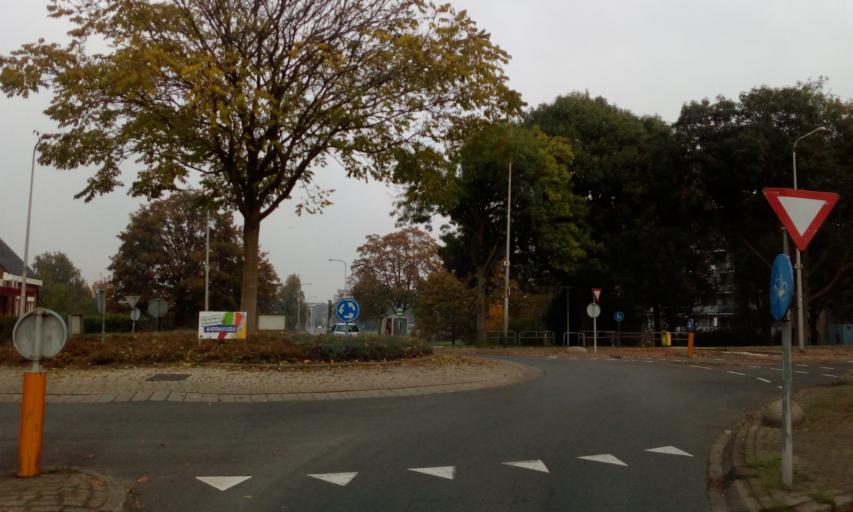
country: NL
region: South Holland
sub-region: Gemeente Waddinxveen
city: Groenswaard
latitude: 52.0459
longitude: 4.6457
